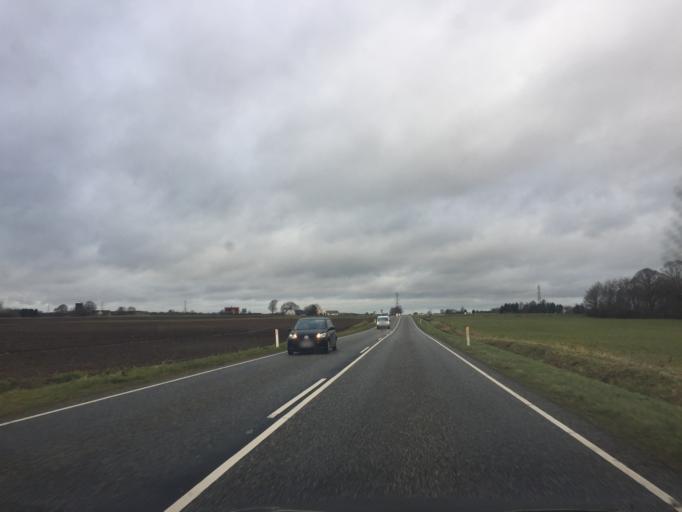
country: DK
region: Zealand
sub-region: Soro Kommune
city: Stenlille
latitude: 55.4868
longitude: 11.5721
